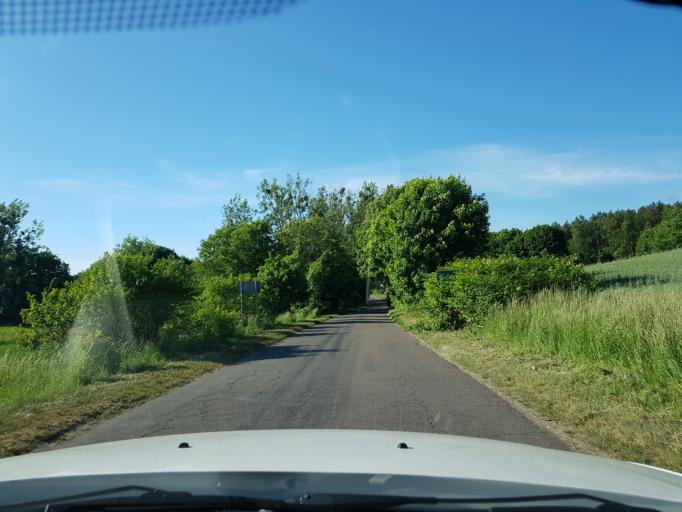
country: PL
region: West Pomeranian Voivodeship
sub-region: Powiat gryfinski
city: Banie
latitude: 53.1984
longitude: 14.6204
